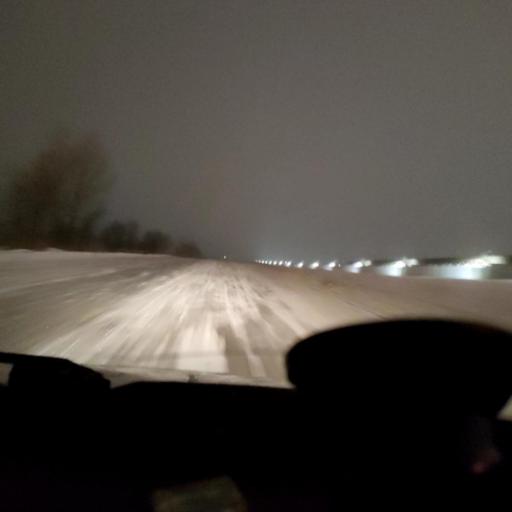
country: RU
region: Perm
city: Gamovo
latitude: 57.9168
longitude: 56.1086
